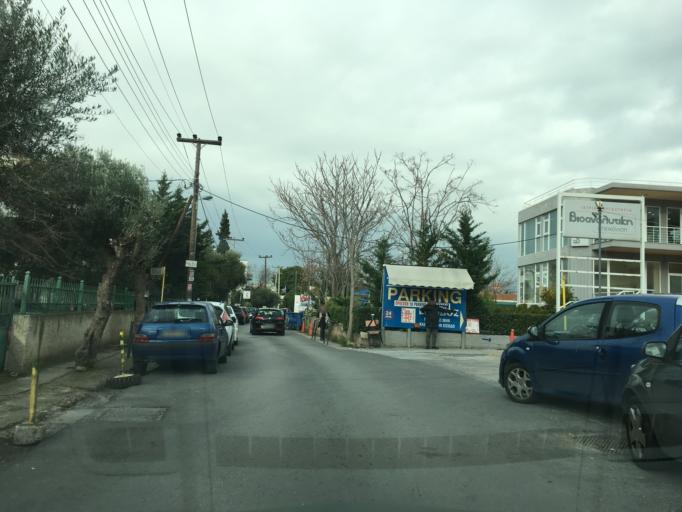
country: GR
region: Attica
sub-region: Nomarchia Athinas
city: Filothei
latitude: 38.0291
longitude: 23.7885
